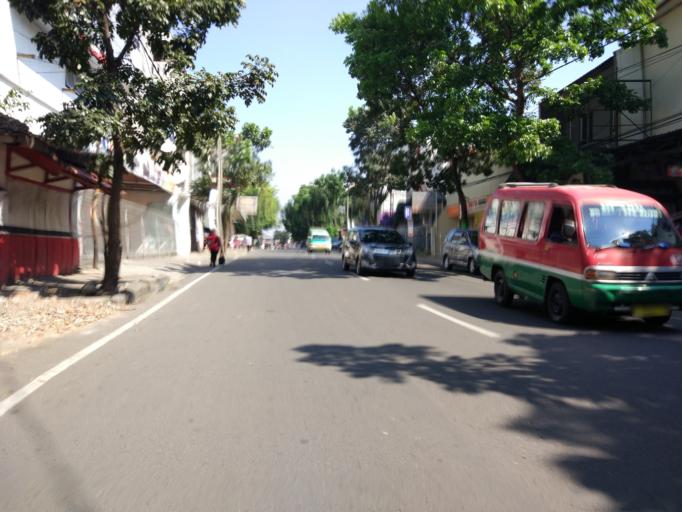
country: ID
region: West Java
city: Bandung
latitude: -6.9317
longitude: 107.6053
